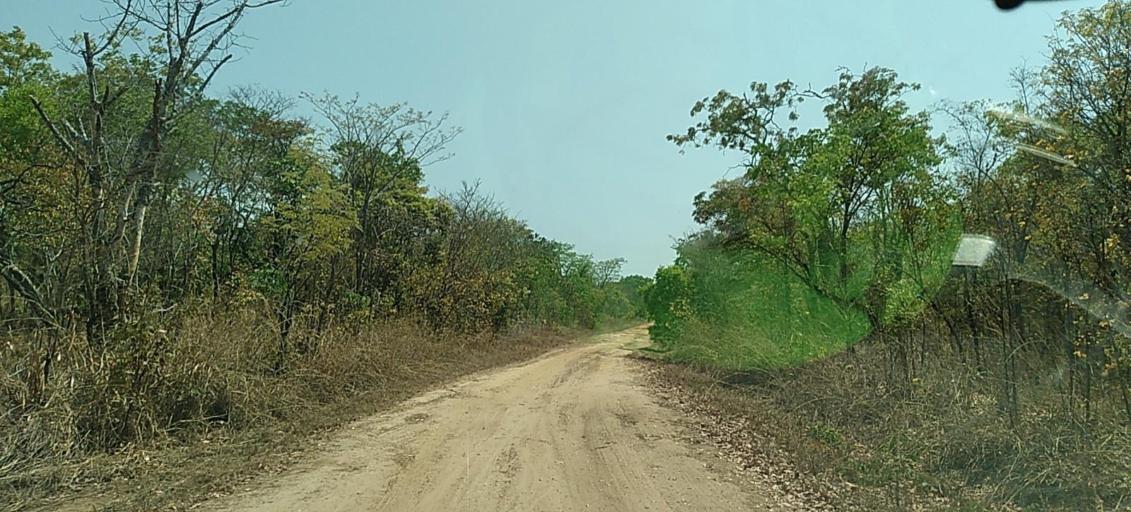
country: ZM
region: North-Western
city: Kalengwa
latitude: -13.1080
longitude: 24.6907
